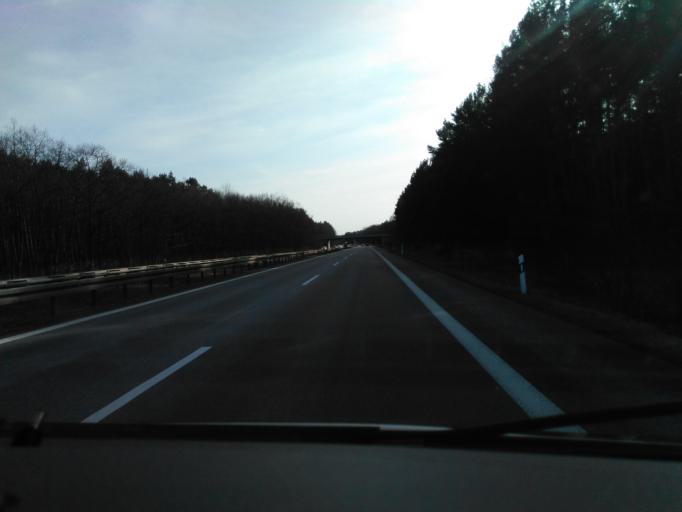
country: DE
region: Brandenburg
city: Bronkow
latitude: 51.6832
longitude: 13.9008
